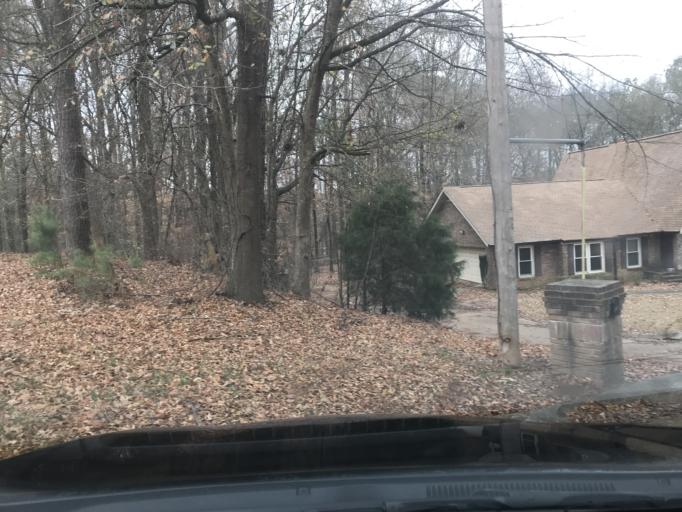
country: US
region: Georgia
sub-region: Fulton County
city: East Point
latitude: 33.7197
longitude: -84.5004
